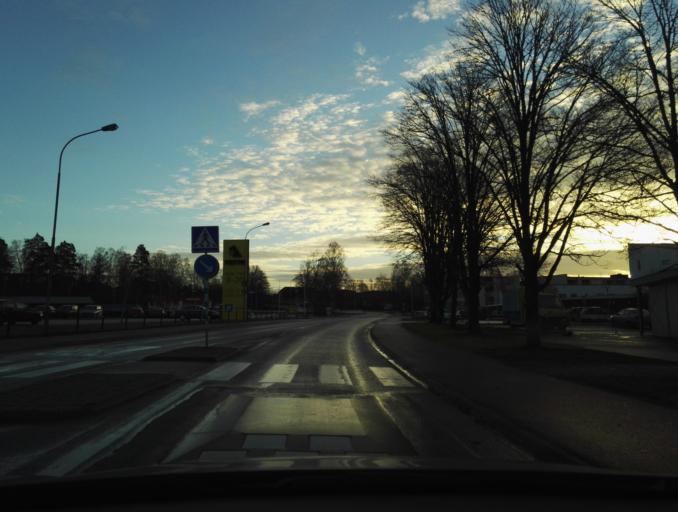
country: SE
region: Kronoberg
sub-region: Vaxjo Kommun
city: Vaexjoe
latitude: 56.8998
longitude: 14.7957
